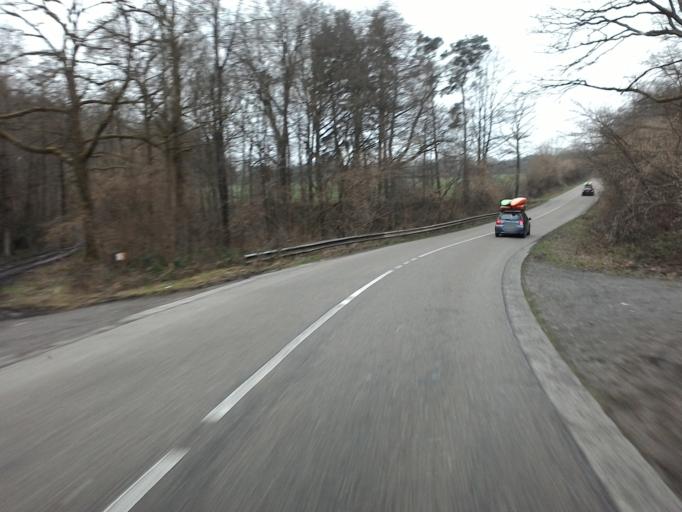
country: BE
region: Wallonia
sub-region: Province de Namur
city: Gedinne
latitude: 50.0394
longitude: 4.9624
